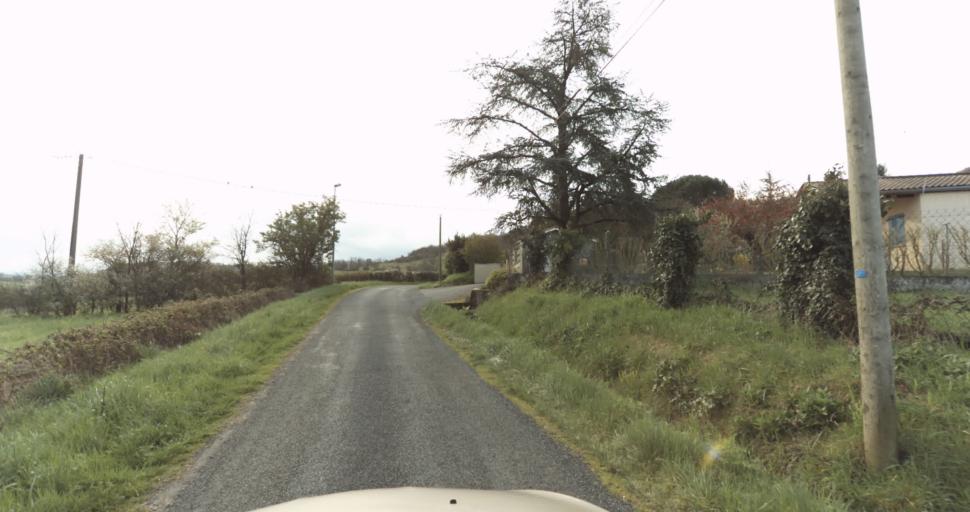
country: FR
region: Midi-Pyrenees
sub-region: Departement du Tarn
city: Puygouzon
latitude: 43.9067
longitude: 2.1752
